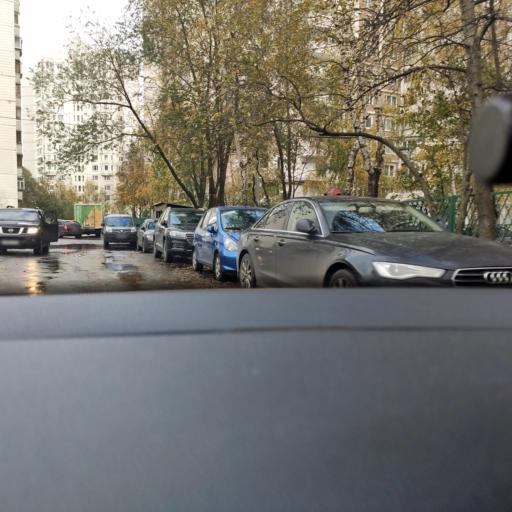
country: RU
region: Moskovskaya
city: Shcherbinka
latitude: 55.5497
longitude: 37.5531
